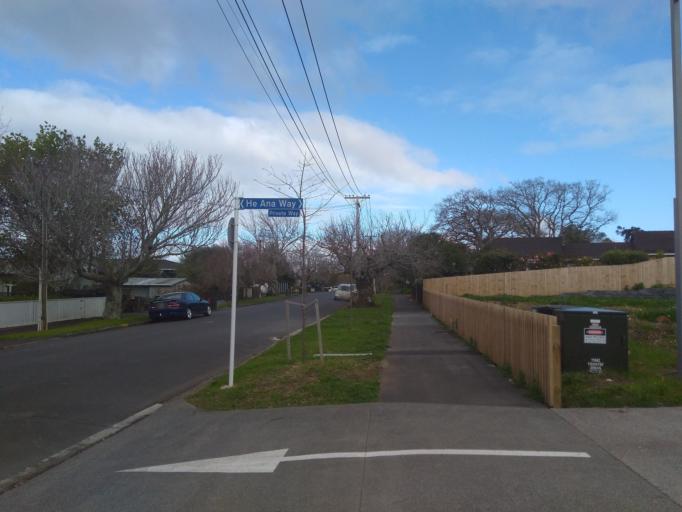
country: NZ
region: Auckland
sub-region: Auckland
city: Auckland
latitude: -36.8795
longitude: 174.7215
